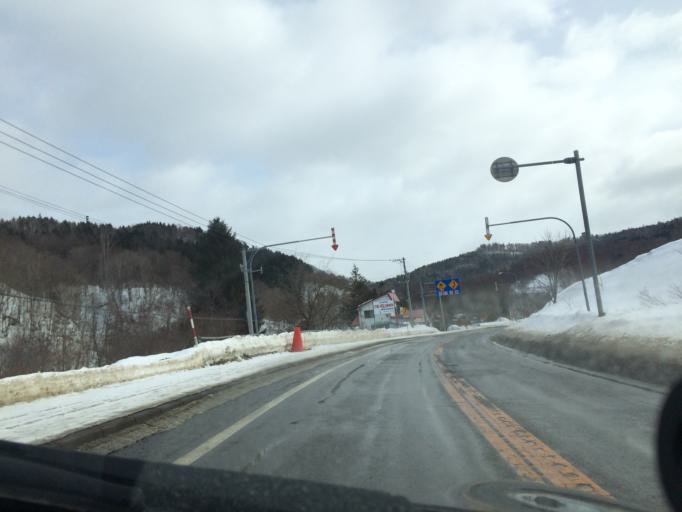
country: JP
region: Hokkaido
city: Iwamizawa
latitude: 42.9322
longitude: 142.0916
